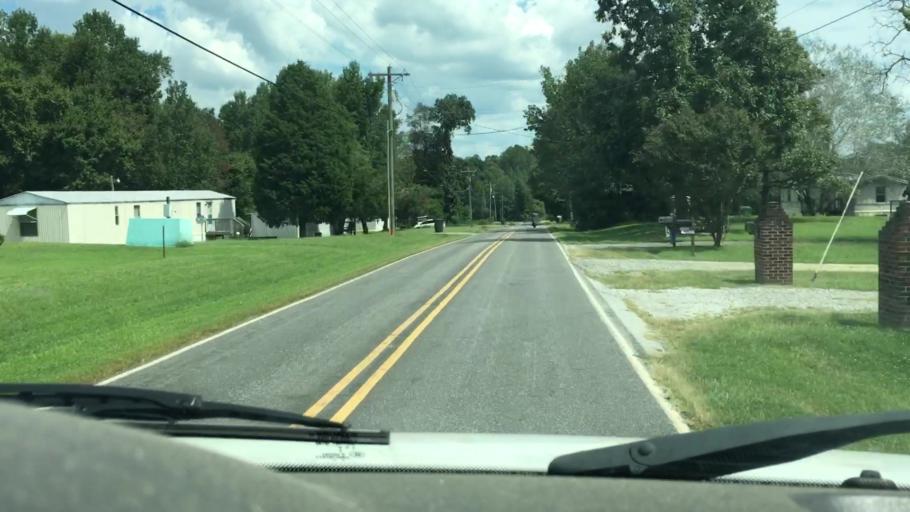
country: US
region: North Carolina
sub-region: Iredell County
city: Mooresville
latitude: 35.6679
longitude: -80.7885
